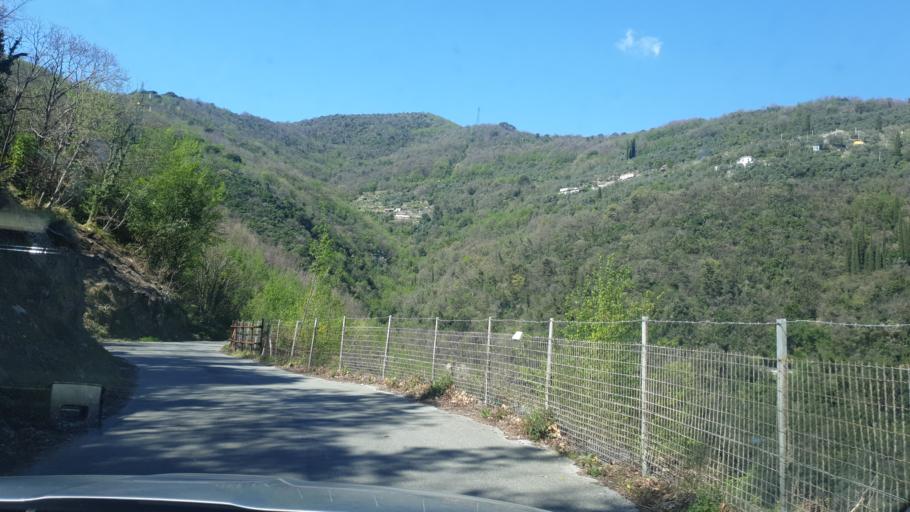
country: IT
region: Liguria
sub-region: Provincia di Genova
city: Recco
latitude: 44.3761
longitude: 9.1449
